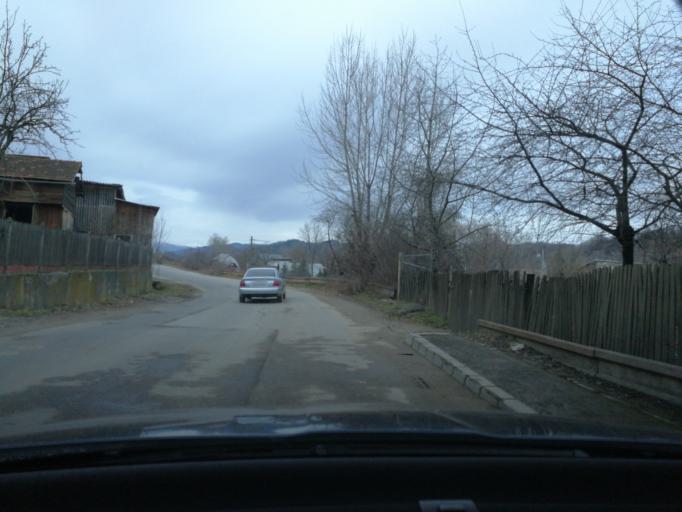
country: RO
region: Prahova
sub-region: Comuna Poiana Campina
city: Poiana Campina
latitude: 45.1426
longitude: 25.6949
